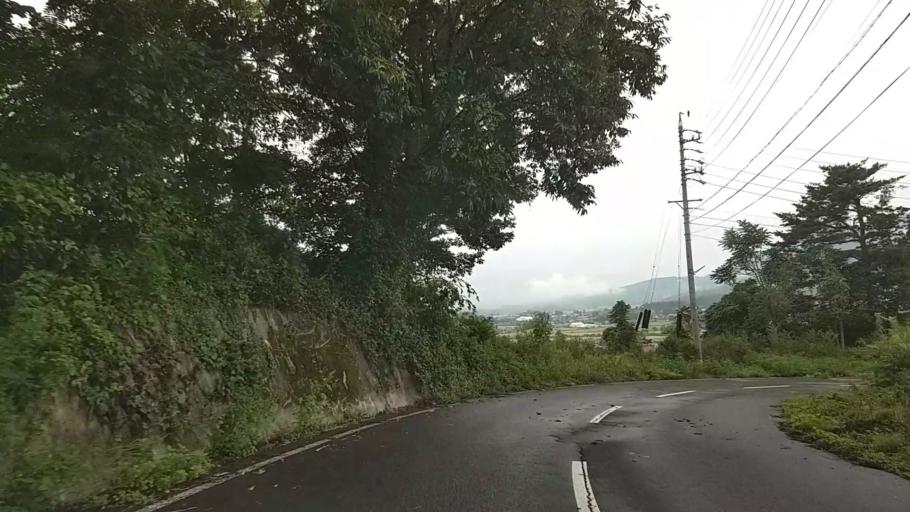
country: JP
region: Nagano
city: Iiyama
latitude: 36.8305
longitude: 138.4083
